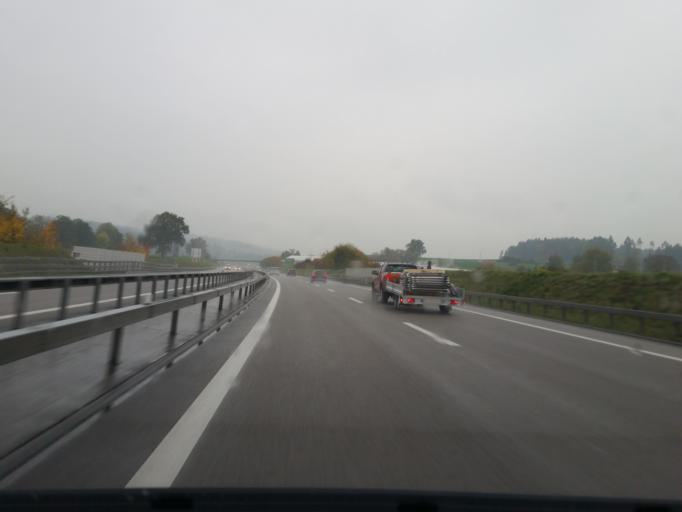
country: CH
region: Thurgau
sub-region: Frauenfeld District
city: Gachnang
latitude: 47.5503
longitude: 8.8277
